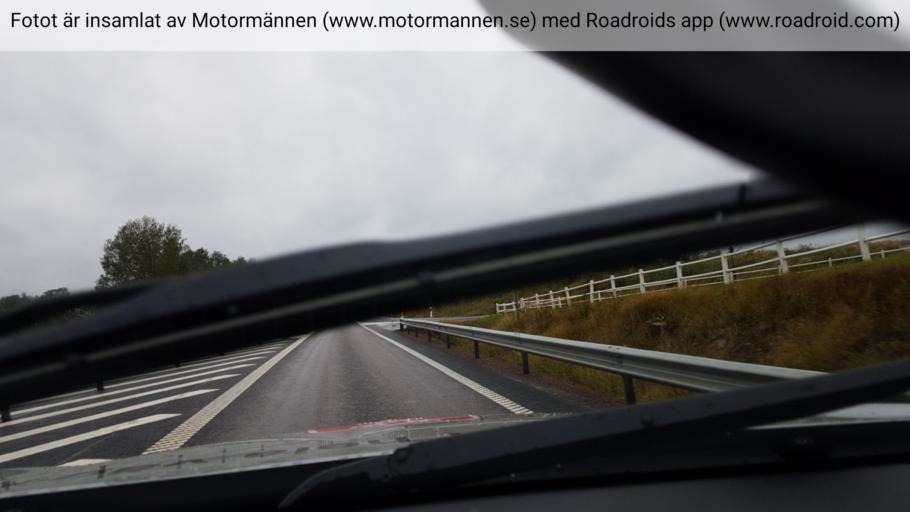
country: SE
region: Vaestra Goetaland
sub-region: Amals Kommun
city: Amal
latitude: 58.9670
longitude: 12.6161
